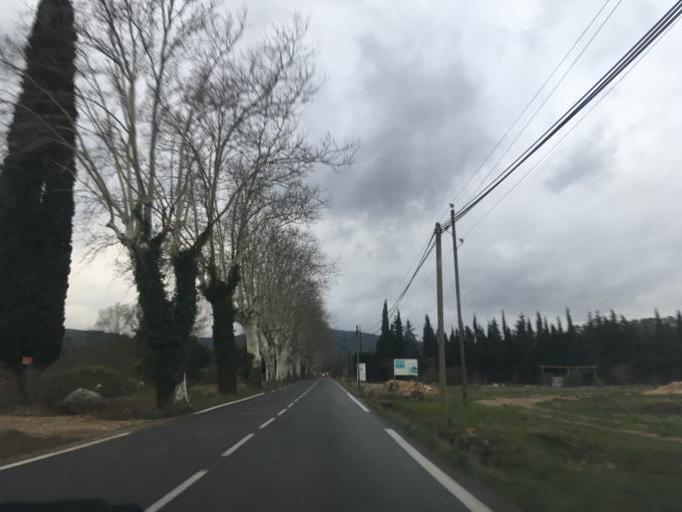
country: FR
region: Provence-Alpes-Cote d'Azur
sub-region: Departement du Var
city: Besse-sur-Issole
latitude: 43.3442
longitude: 6.1713
